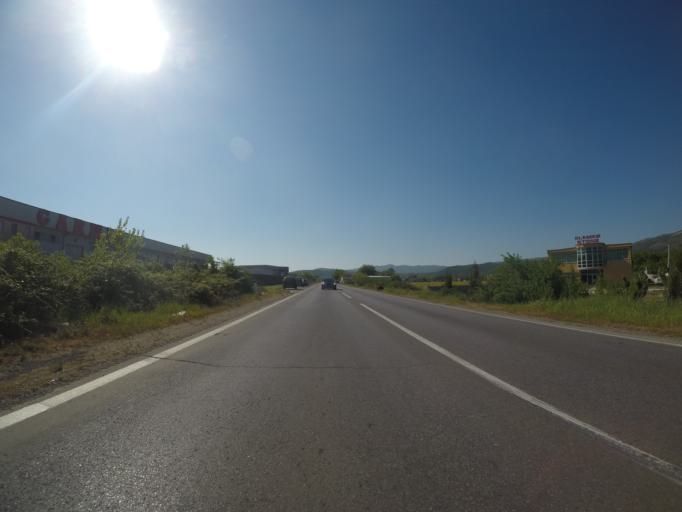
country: ME
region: Danilovgrad
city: Danilovgrad
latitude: 42.5333
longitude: 19.1148
